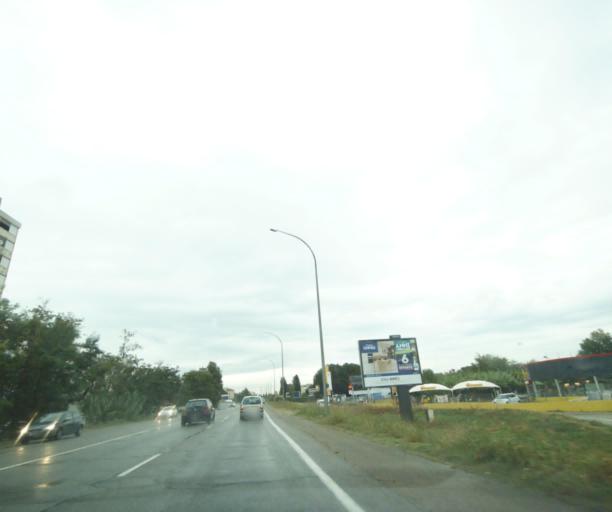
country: FR
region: Languedoc-Roussillon
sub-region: Departement du Gard
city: Rodilhan
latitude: 43.8427
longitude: 4.3914
